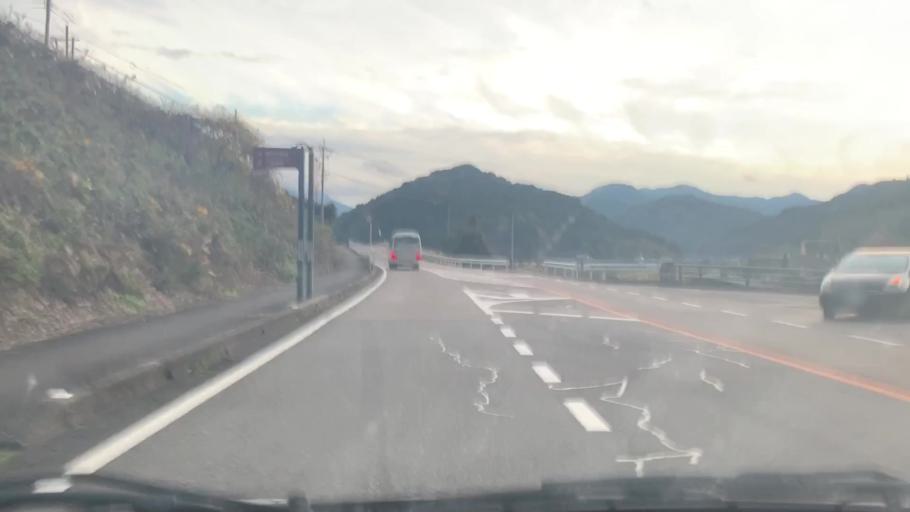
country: JP
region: Saga Prefecture
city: Kashima
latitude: 33.0777
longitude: 130.0673
